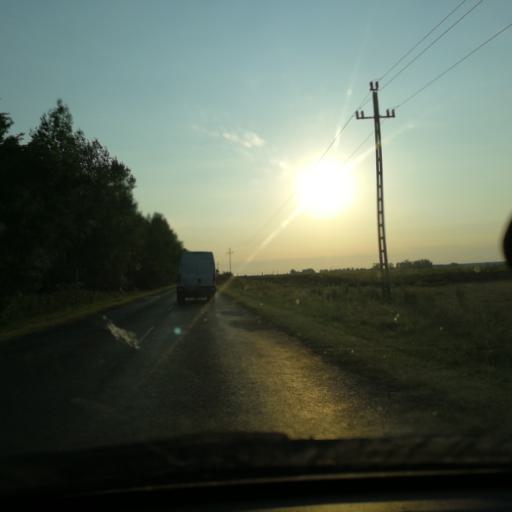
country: HU
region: Bacs-Kiskun
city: Kiskunhalas
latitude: 46.4423
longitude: 19.5879
